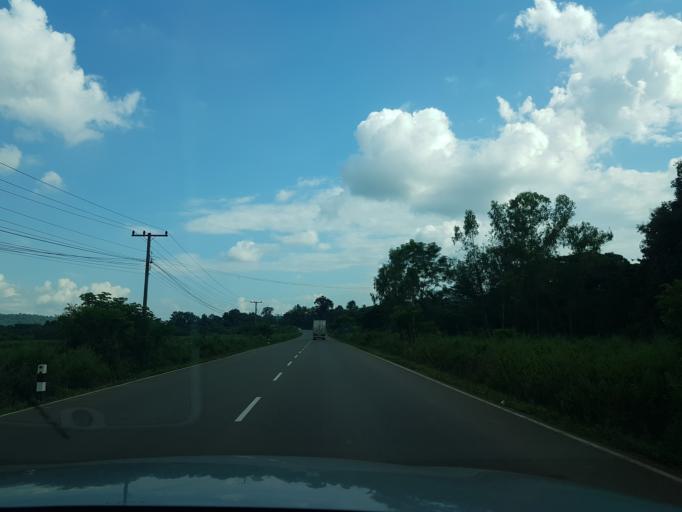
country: TH
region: Nong Khai
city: Sangkhom
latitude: 18.0283
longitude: 102.3761
